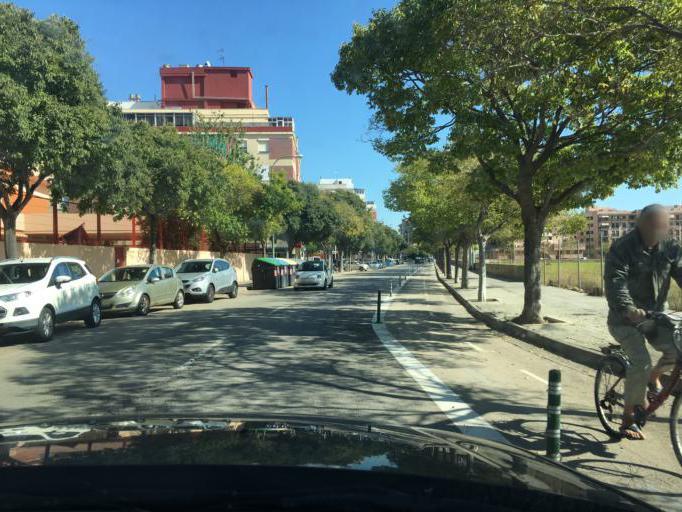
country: ES
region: Balearic Islands
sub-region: Illes Balears
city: Palma
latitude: 39.5820
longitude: 2.6802
